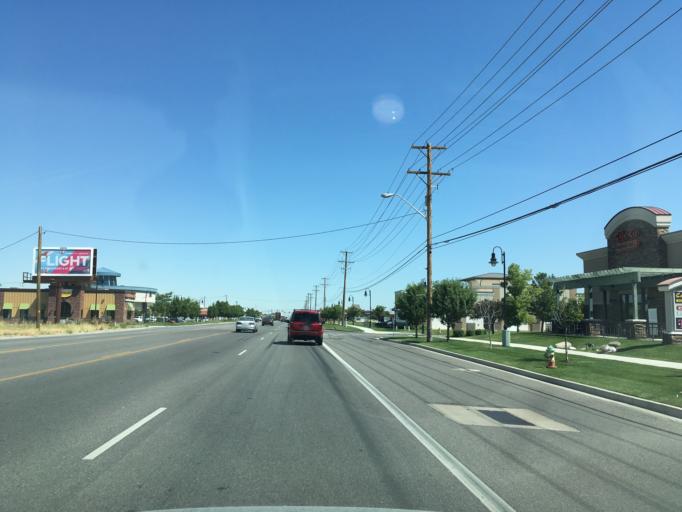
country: US
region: Utah
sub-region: Salt Lake County
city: West Valley City
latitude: 40.7074
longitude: -112.0249
